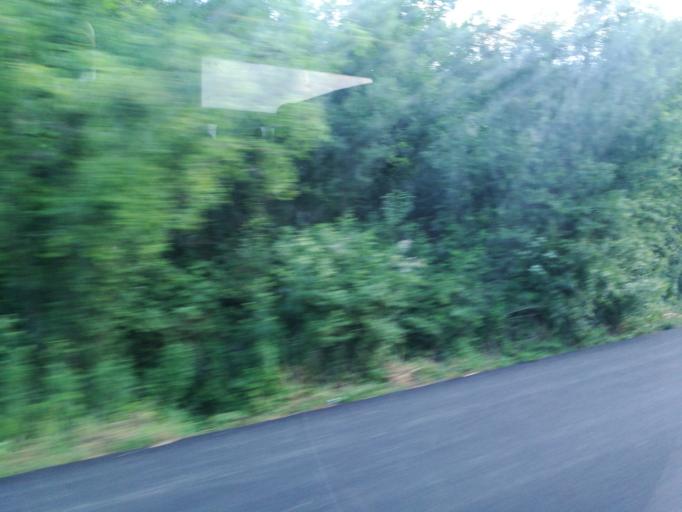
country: RO
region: Dambovita
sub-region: Comuna Branistea
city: Dambovicioara
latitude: 44.6656
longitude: 25.5418
